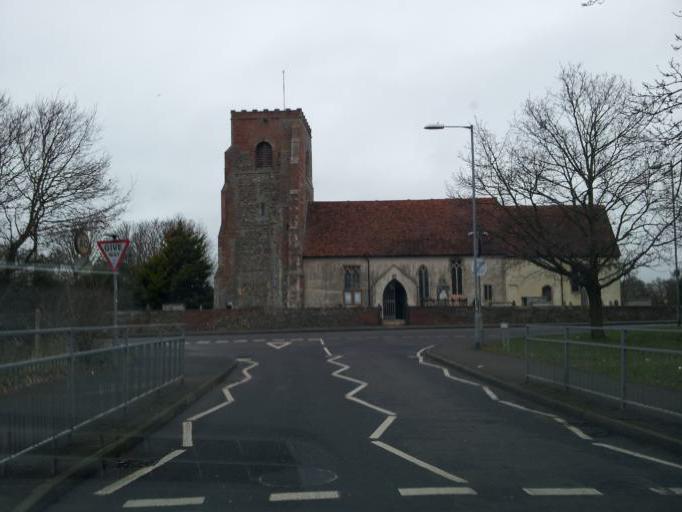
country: GB
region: England
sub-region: Suffolk
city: Shotley Gate
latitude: 51.9278
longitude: 1.2251
